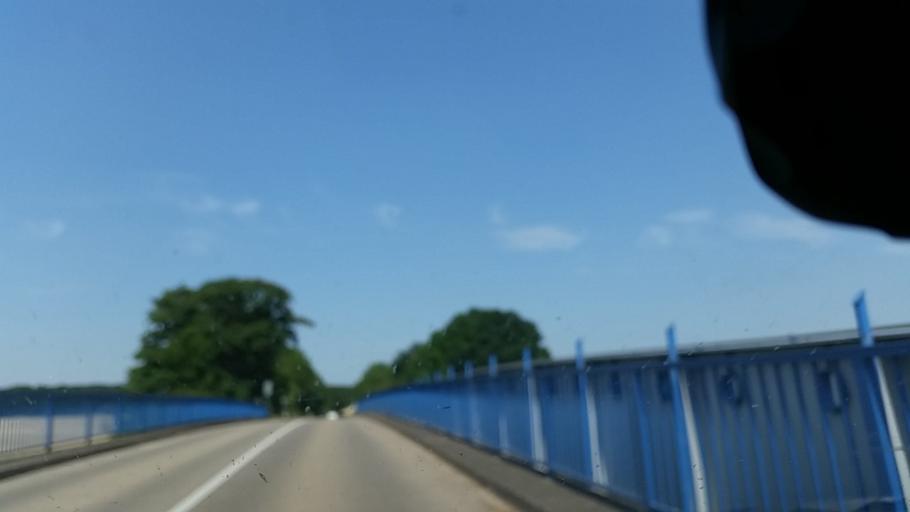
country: DE
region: Lower Saxony
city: Langwedel
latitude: 52.9690
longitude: 9.1561
